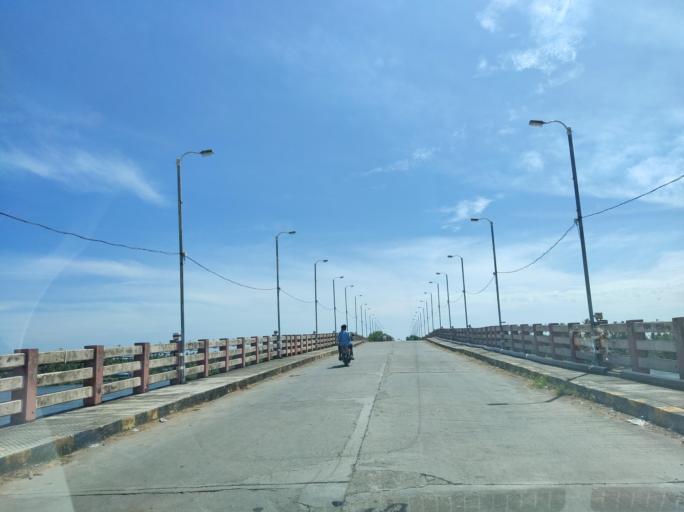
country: IN
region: Kerala
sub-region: Alappuzha
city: Kayankulam
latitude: 9.1685
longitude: 76.4579
